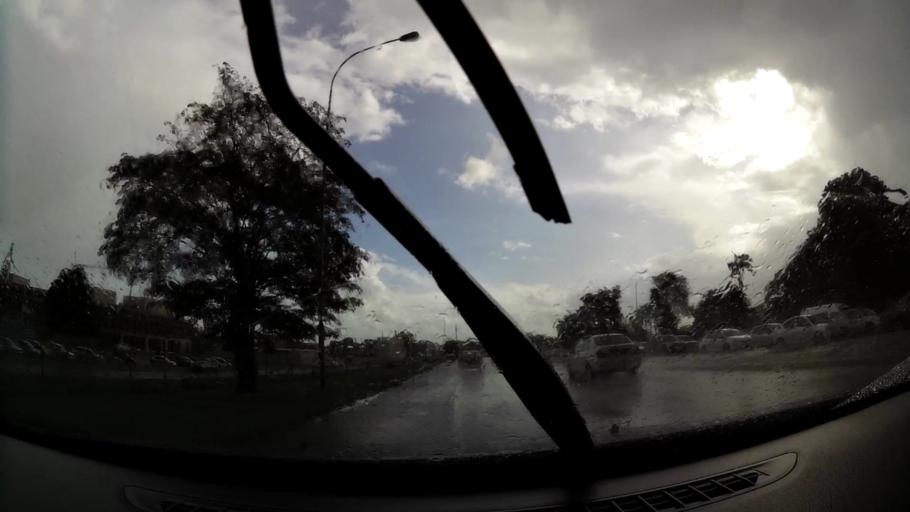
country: TT
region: Tunapuna/Piarco
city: Tunapuna
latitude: 10.6473
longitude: -61.4258
